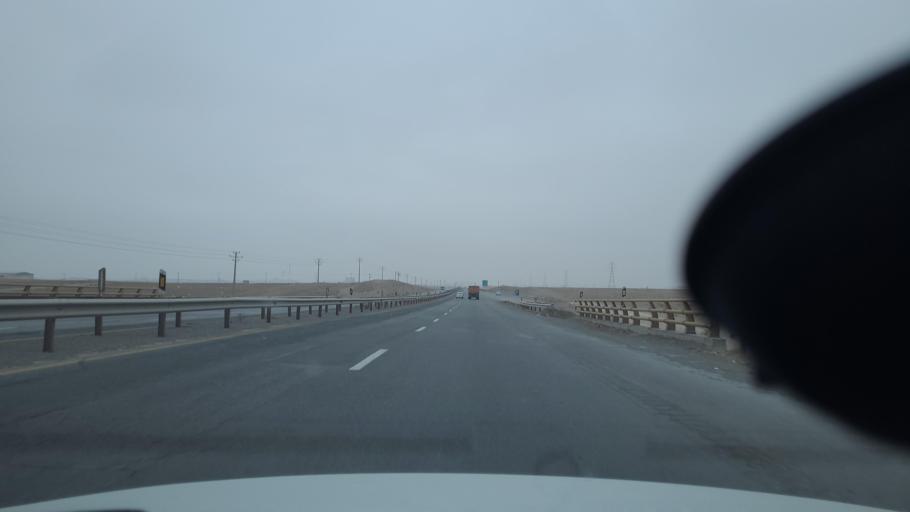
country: IR
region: Razavi Khorasan
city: Fariman
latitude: 35.9609
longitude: 59.7471
